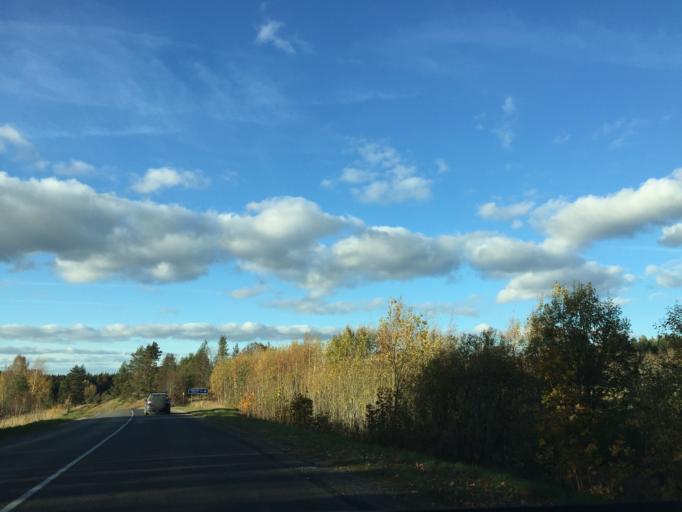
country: LV
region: Tukuma Rajons
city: Tukums
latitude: 57.0004
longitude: 23.0844
